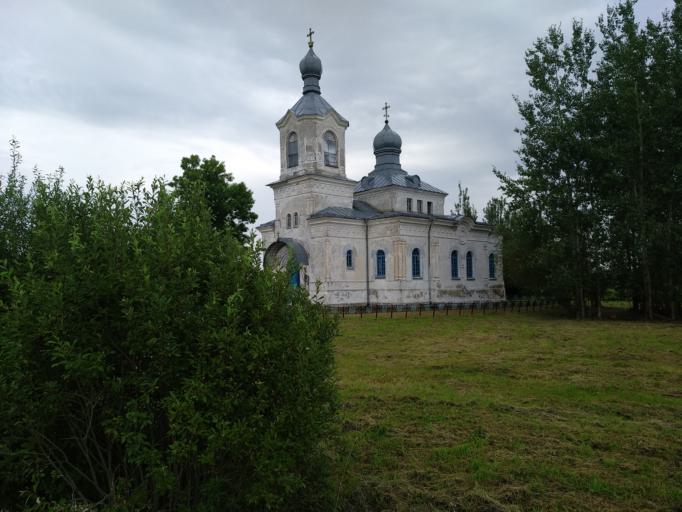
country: BY
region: Vitebsk
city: Sharkawshchyna
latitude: 55.3087
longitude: 27.2584
